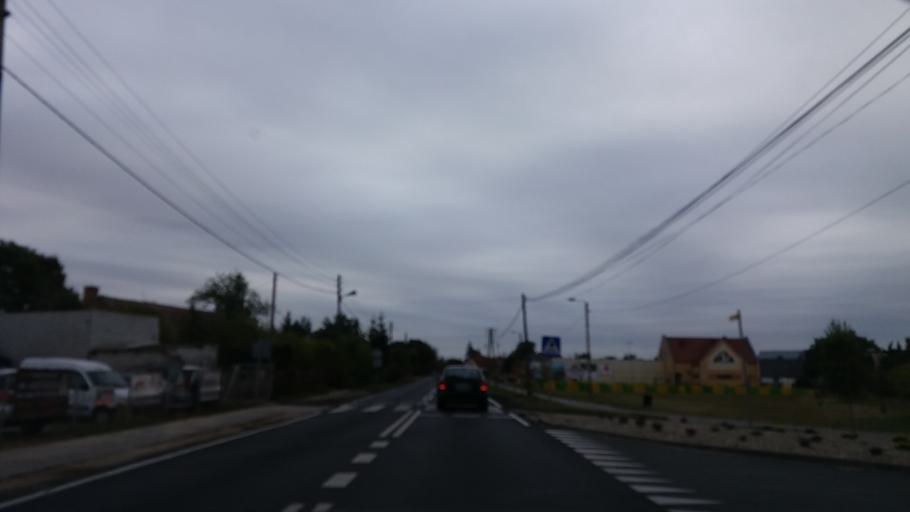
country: PL
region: Lubusz
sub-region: Powiat gorzowski
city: Klodawa
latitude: 52.7852
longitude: 15.2147
